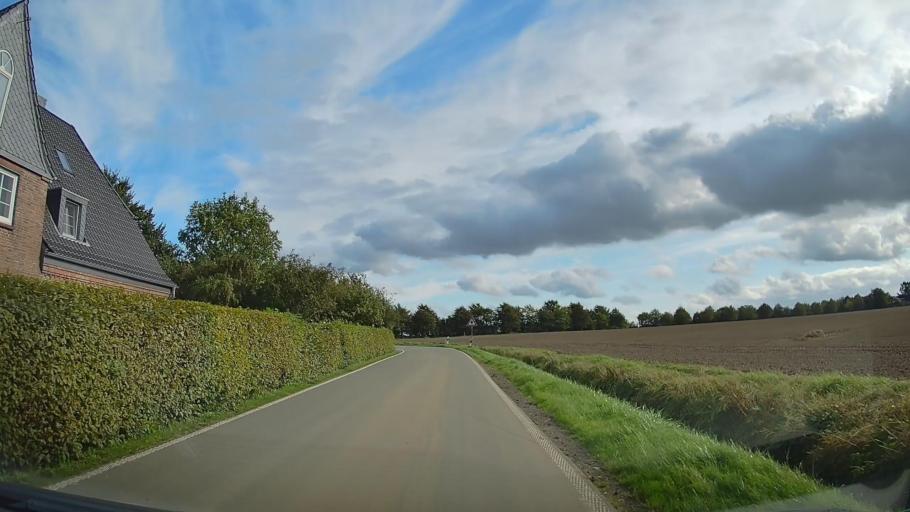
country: DE
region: Schleswig-Holstein
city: Steinbergkirche
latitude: 54.8017
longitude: 9.7427
